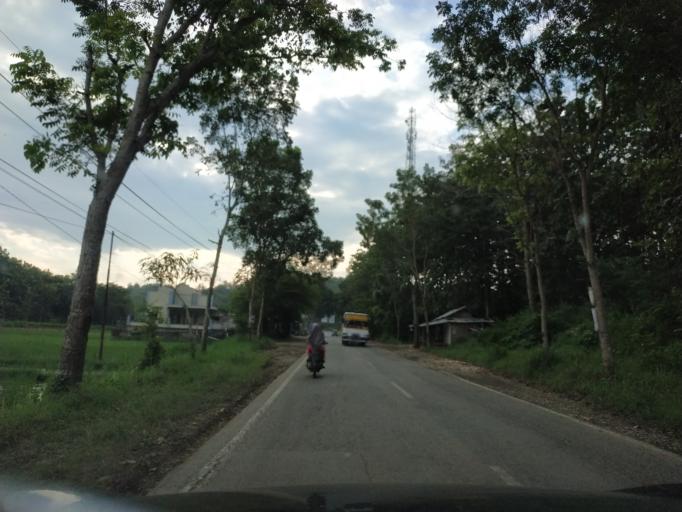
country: ID
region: Central Java
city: Ngampel
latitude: -6.9010
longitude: 111.4413
